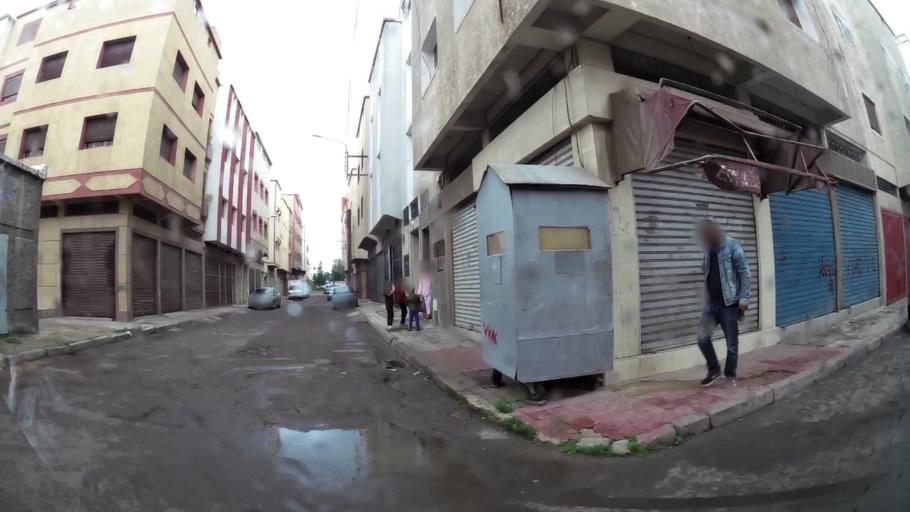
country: MA
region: Grand Casablanca
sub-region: Casablanca
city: Casablanca
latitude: 33.5447
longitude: -7.5850
